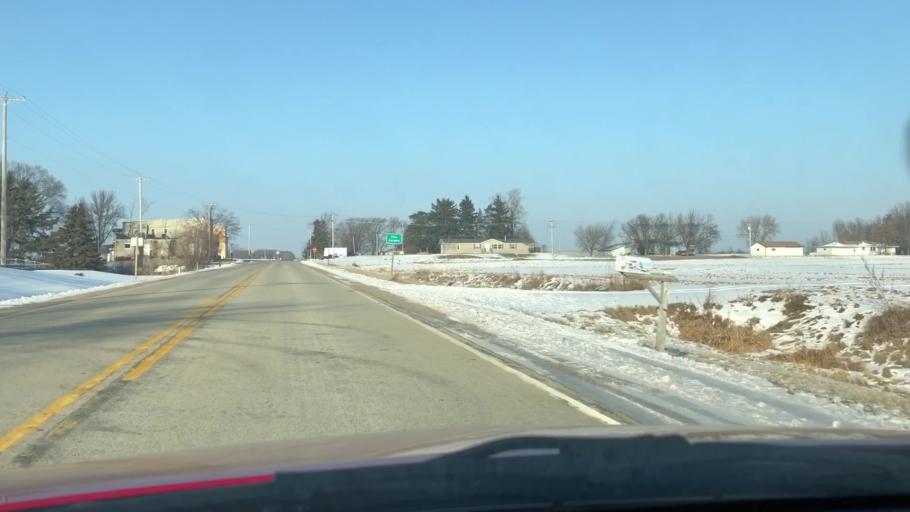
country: US
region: Wisconsin
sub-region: Outagamie County
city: Black Creek
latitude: 44.4130
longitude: -88.3743
